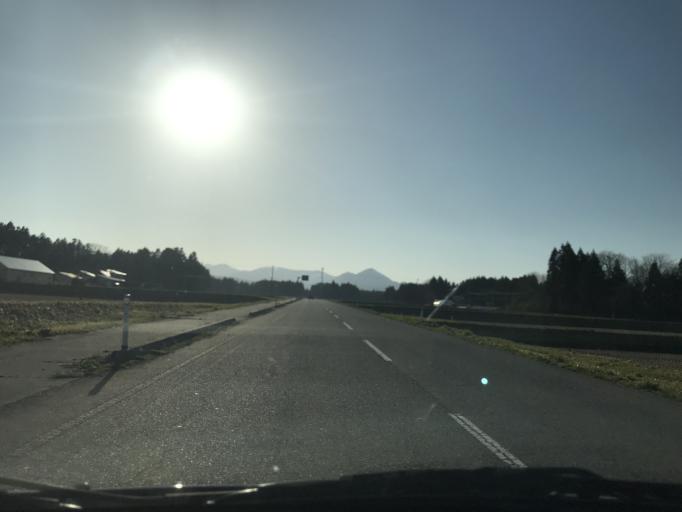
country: JP
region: Iwate
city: Kitakami
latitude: 39.2376
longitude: 141.0586
